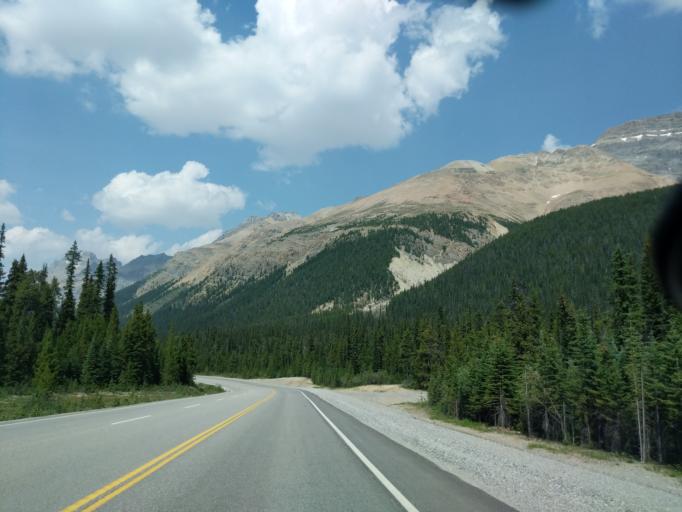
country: CA
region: Alberta
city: Lake Louise
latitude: 51.7274
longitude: -116.5010
